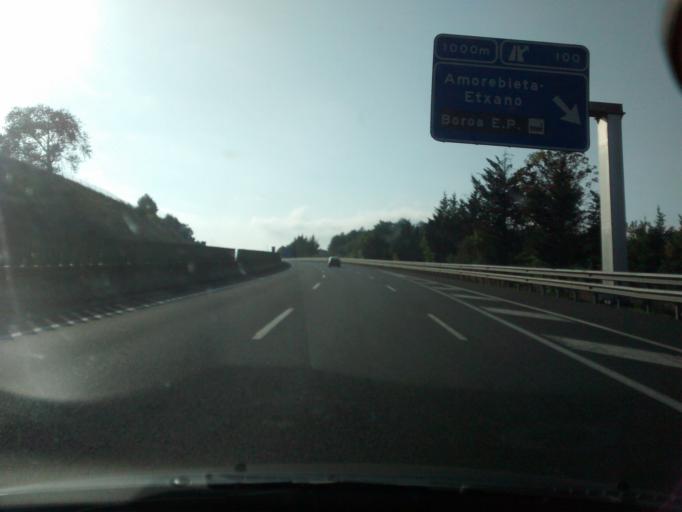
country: ES
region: Basque Country
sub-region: Bizkaia
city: Amorebieta
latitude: 43.2258
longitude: -2.7375
